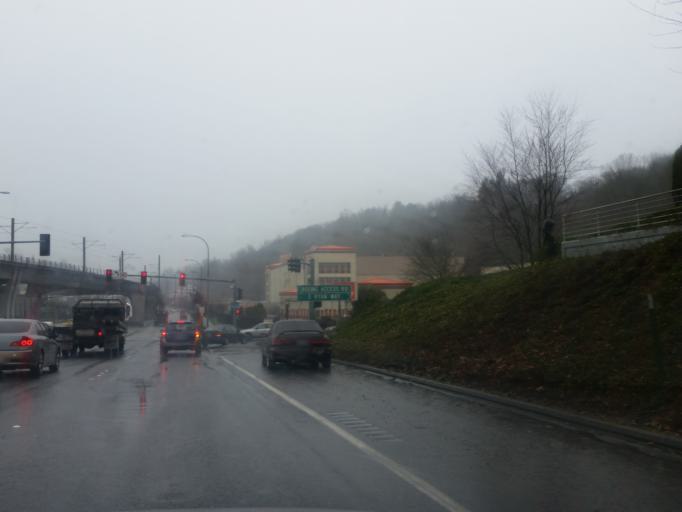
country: US
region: Washington
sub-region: King County
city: Riverton
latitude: 47.5075
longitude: -122.2782
